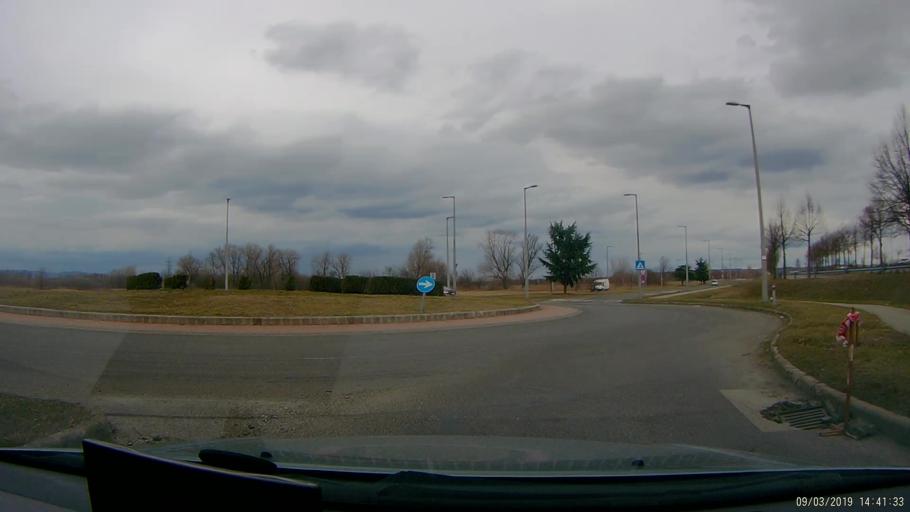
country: HU
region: Budapest
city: Budapest XV. keruelet
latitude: 47.5806
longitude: 19.1597
